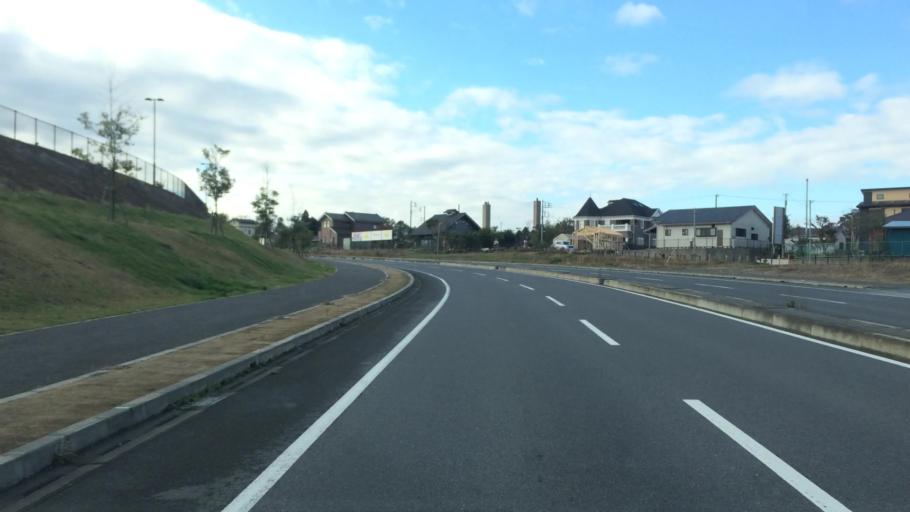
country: JP
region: Chiba
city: Shisui
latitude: 35.7159
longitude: 140.2930
